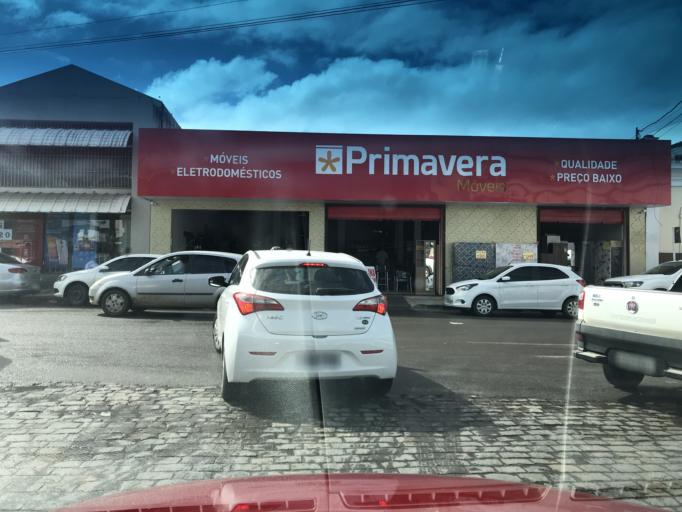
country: BR
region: Bahia
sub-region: Santo Antonio De Jesus
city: Santo Antonio de Jesus
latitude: -12.9664
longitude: -39.2633
